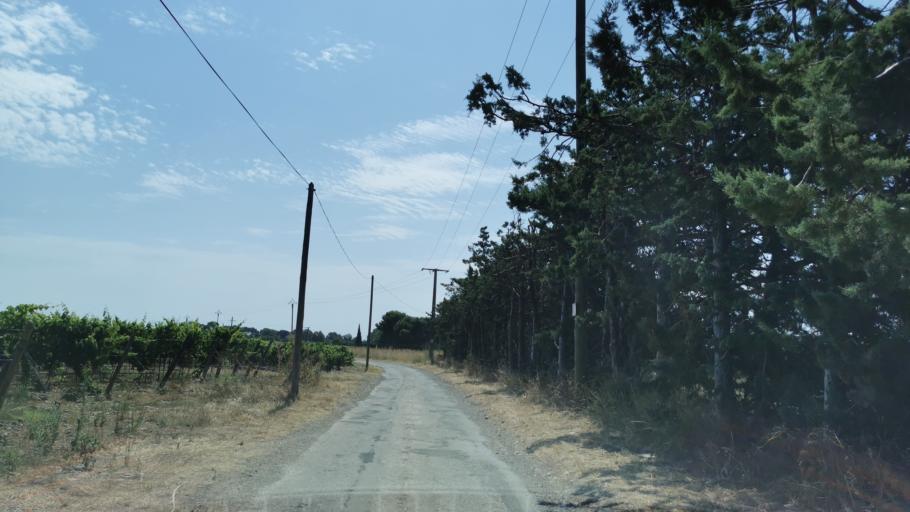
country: FR
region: Languedoc-Roussillon
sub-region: Departement de l'Aude
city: Argeliers
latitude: 43.2897
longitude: 2.8918
